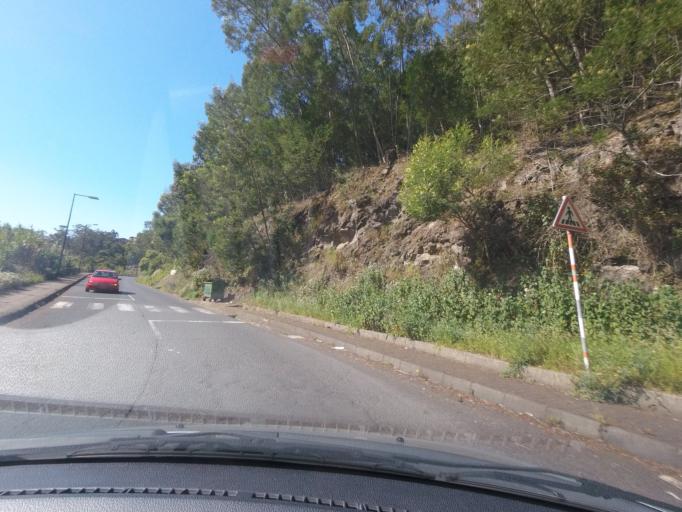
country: PT
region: Madeira
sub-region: Santa Cruz
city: Camacha
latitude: 32.6601
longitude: -16.8522
